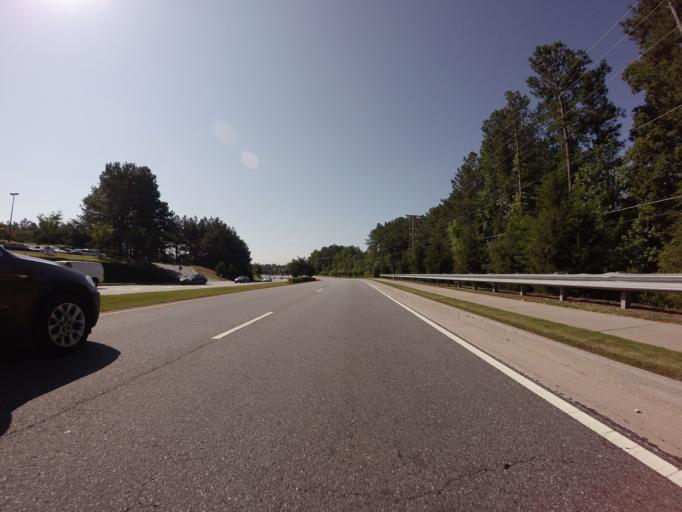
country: US
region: Georgia
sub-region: Fulton County
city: Johns Creek
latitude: 34.0642
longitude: -84.1610
